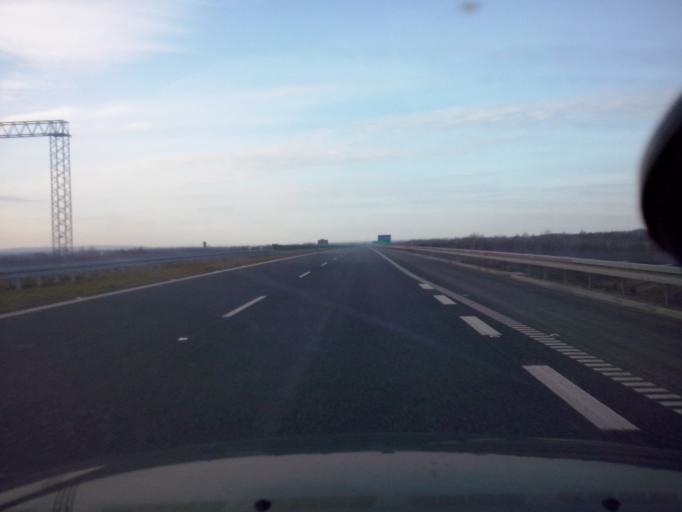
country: PL
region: Subcarpathian Voivodeship
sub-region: Powiat rzeszowski
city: Rudna Mala
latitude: 50.1076
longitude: 21.9731
